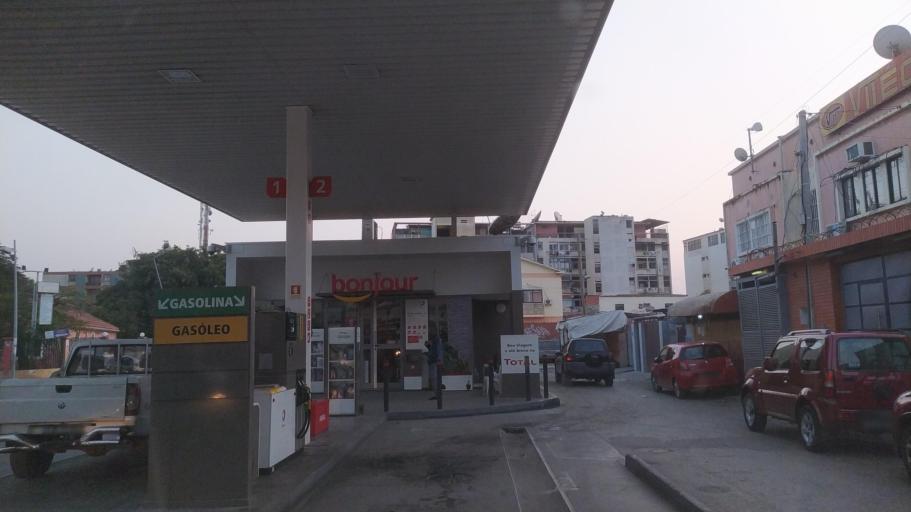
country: AO
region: Luanda
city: Luanda
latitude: -8.8177
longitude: 13.2499
